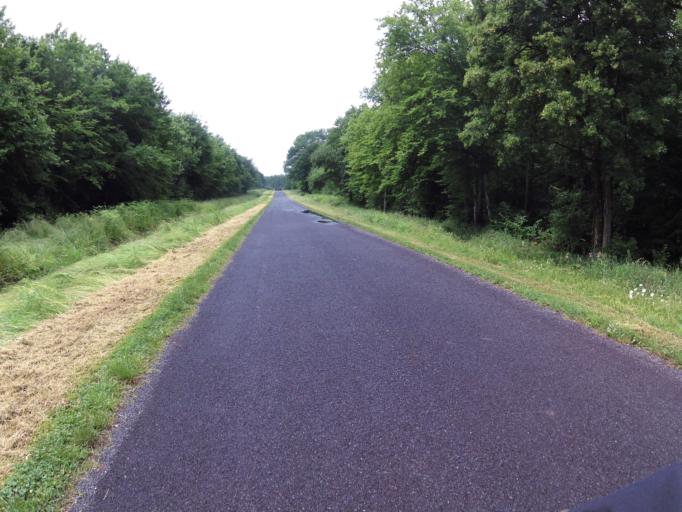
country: FR
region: Champagne-Ardenne
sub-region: Departement de la Marne
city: Sermaize-les-Bains
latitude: 48.7696
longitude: 4.9365
